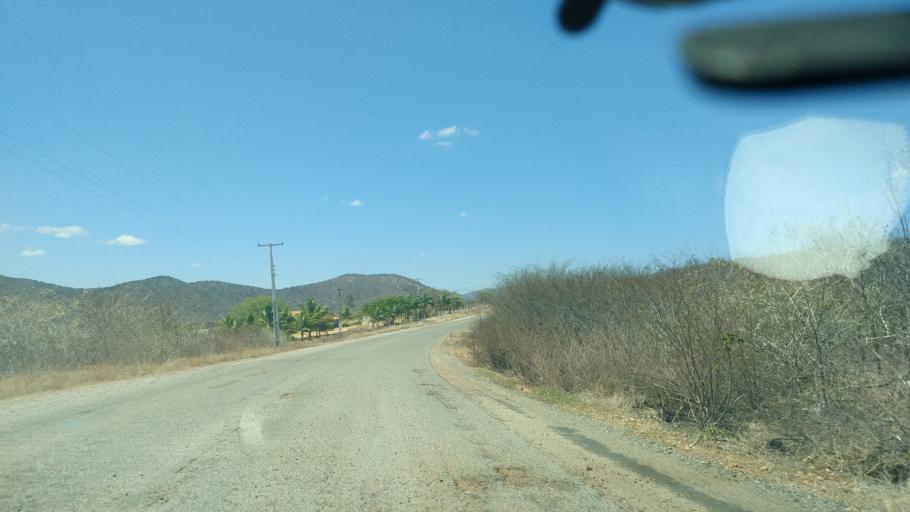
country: BR
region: Rio Grande do Norte
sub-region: Sao Tome
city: Sao Tome
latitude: -5.9769
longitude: -36.1447
